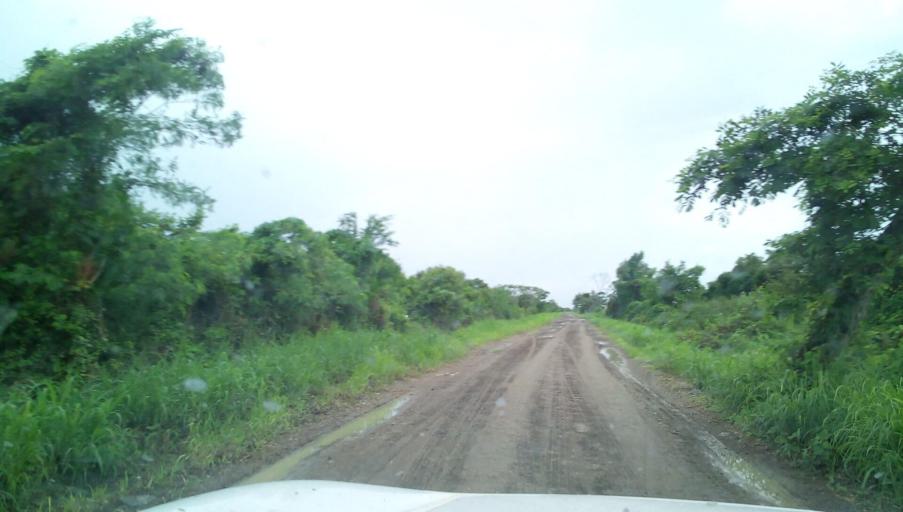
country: MX
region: Veracruz
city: Panuco
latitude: 21.8328
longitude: -98.1105
